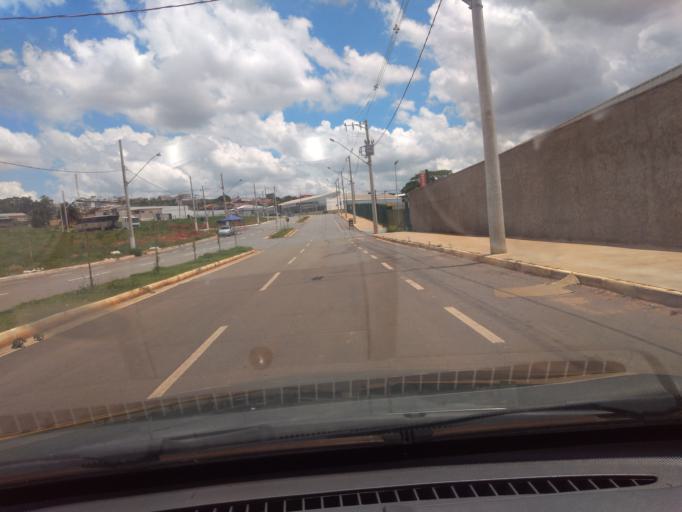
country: BR
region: Minas Gerais
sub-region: Tres Coracoes
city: Tres Coracoes
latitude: -21.6628
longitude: -45.2800
